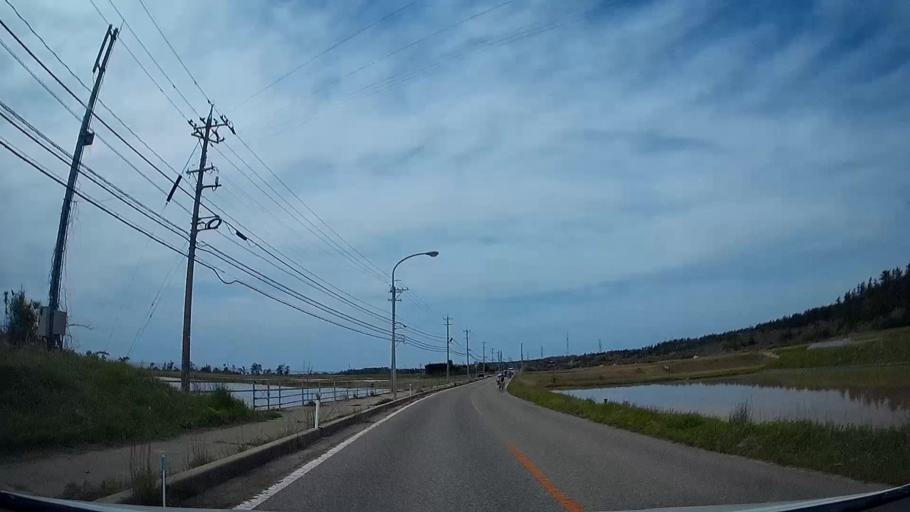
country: JP
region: Ishikawa
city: Hakui
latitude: 37.0396
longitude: 136.7422
